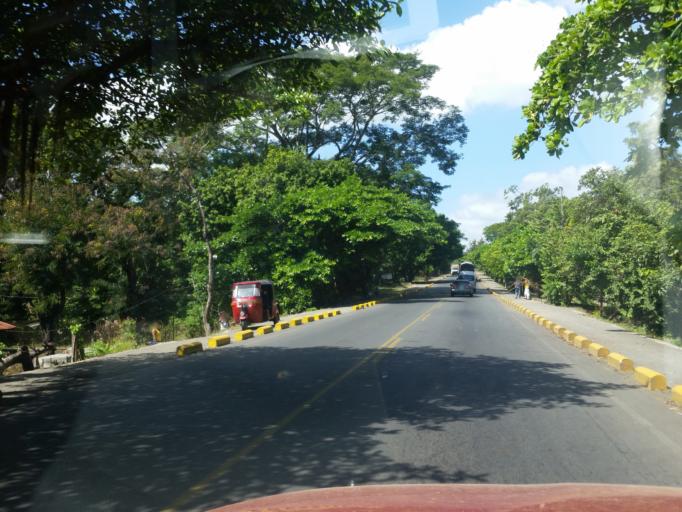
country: NI
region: Granada
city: Diriomo
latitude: 11.8538
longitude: -86.0232
